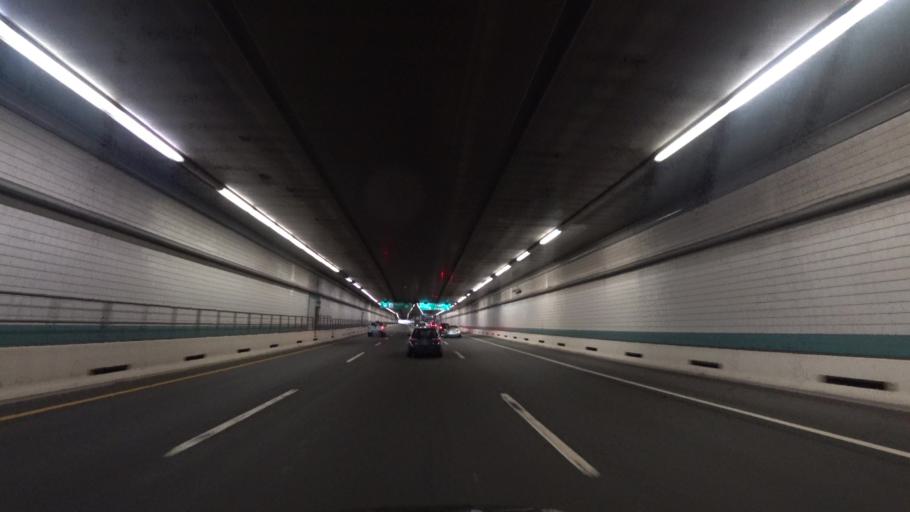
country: US
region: Massachusetts
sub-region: Suffolk County
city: Boston
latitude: 42.3594
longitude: -71.0277
